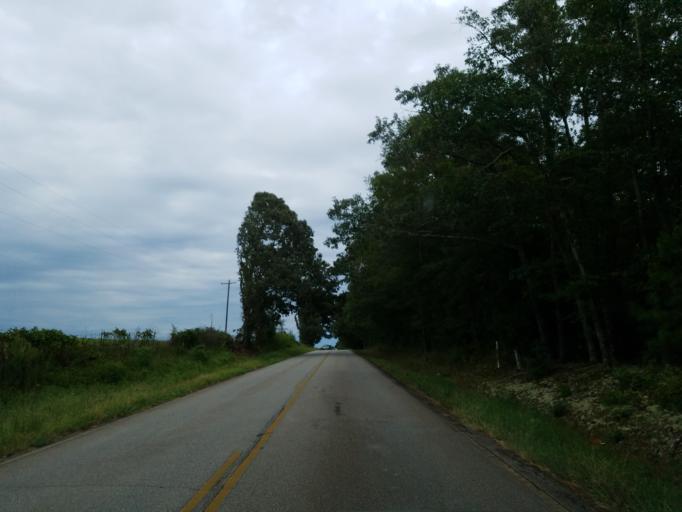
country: US
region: Georgia
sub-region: Monroe County
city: Forsyth
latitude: 32.9885
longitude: -84.0269
